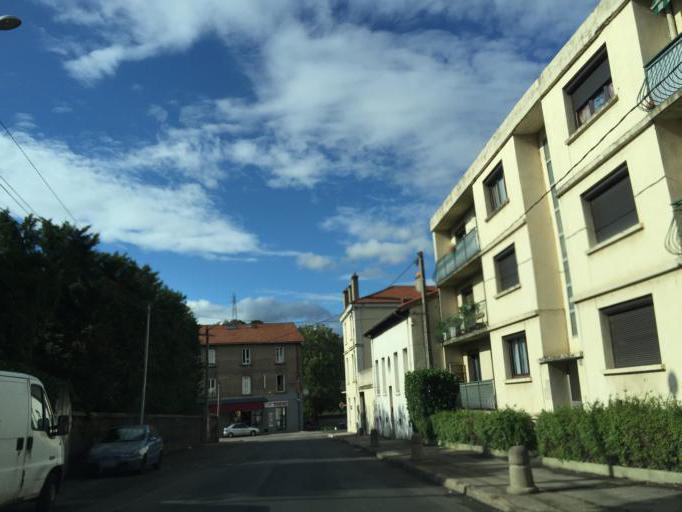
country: FR
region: Rhone-Alpes
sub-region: Departement de la Loire
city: La Grand-Croix
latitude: 45.4891
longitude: 4.5509
